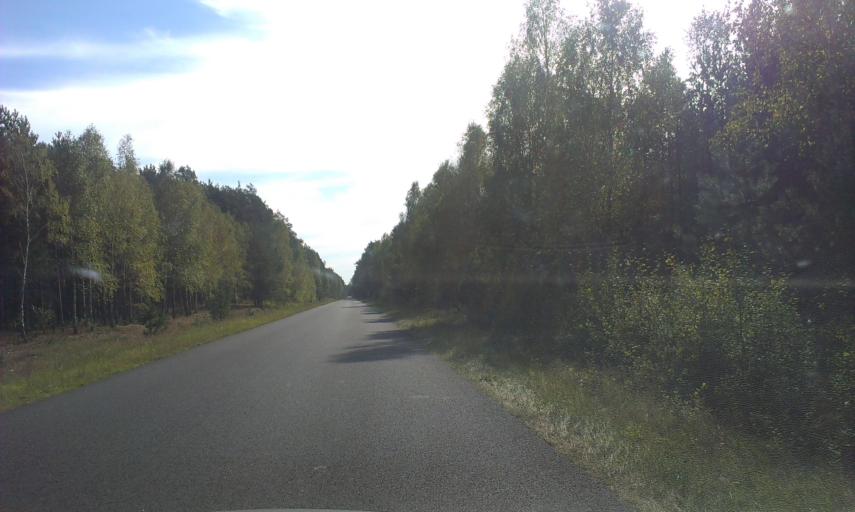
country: PL
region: Greater Poland Voivodeship
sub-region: Powiat zlotowski
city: Okonek
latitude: 53.5255
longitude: 16.9620
